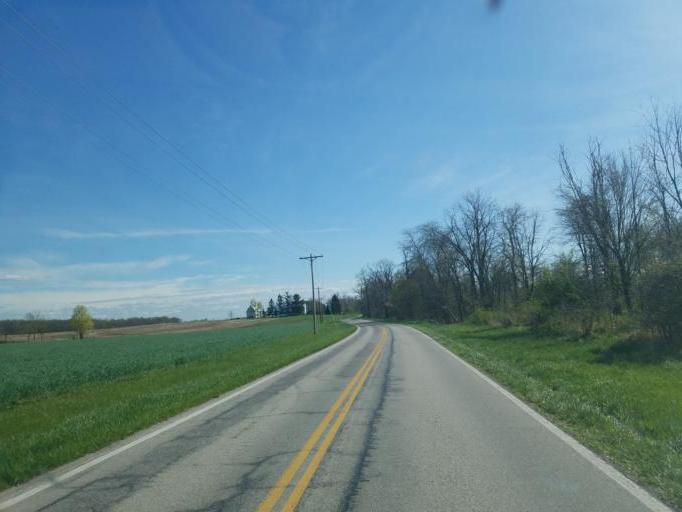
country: US
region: Ohio
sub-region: Huron County
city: Willard
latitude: 41.1046
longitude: -82.7844
